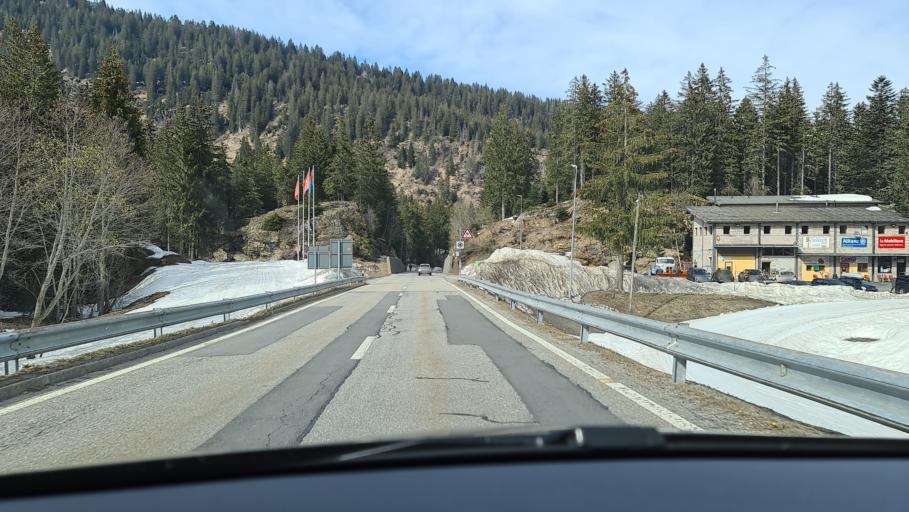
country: CH
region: Ticino
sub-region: Blenio District
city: Cancori
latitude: 46.5178
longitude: 8.8825
